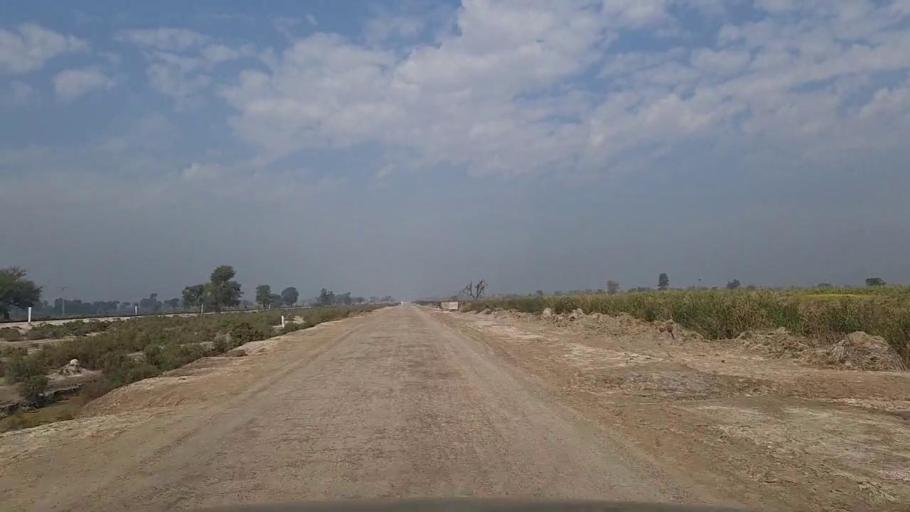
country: PK
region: Sindh
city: Daur
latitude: 26.3743
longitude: 68.3573
